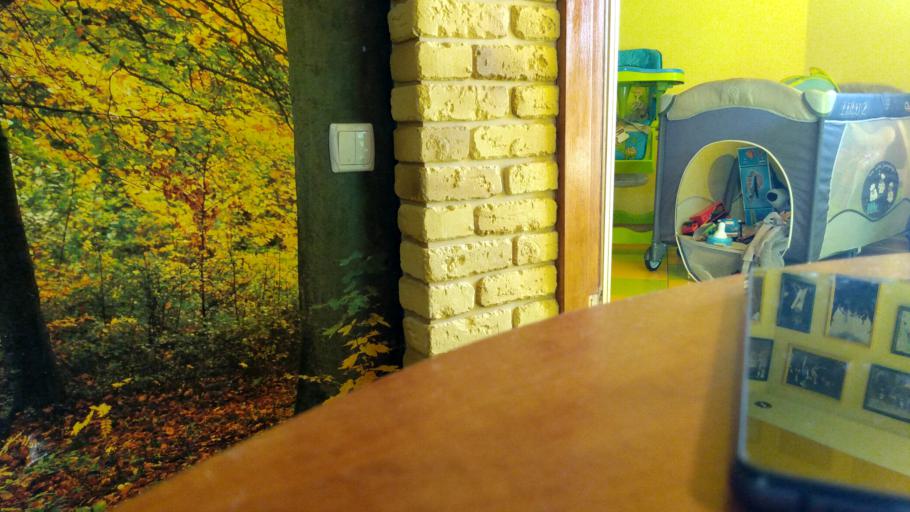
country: RU
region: Tverskaya
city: Likhoslavl'
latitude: 57.1965
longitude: 35.5250
